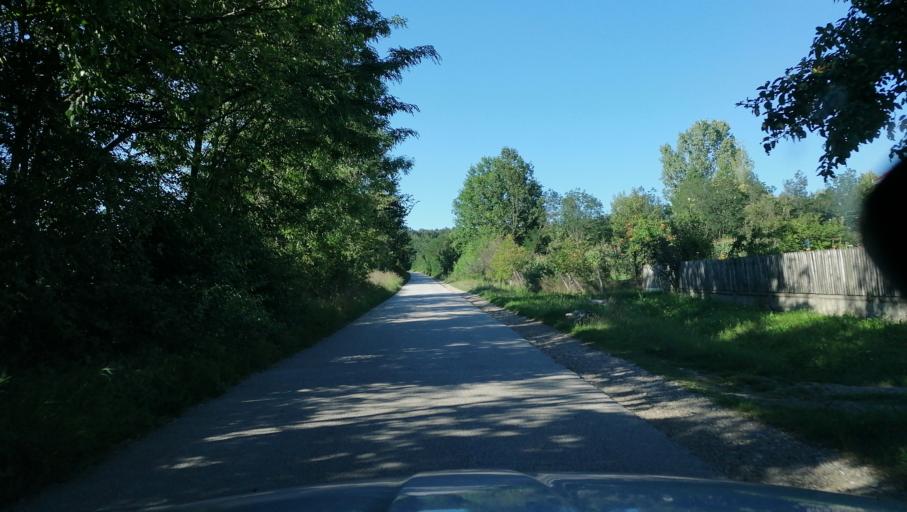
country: RS
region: Central Serbia
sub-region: Sumadijski Okrug
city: Knic
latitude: 43.8863
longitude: 20.6154
